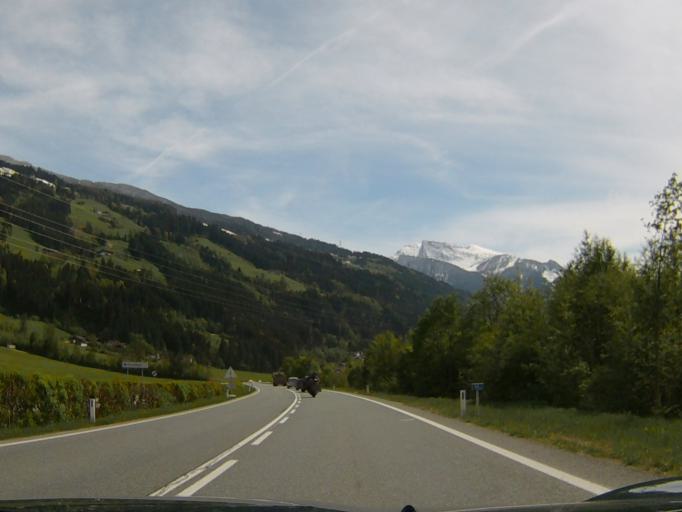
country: AT
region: Tyrol
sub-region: Politischer Bezirk Schwaz
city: Stumm
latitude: 47.2601
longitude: 11.8992
